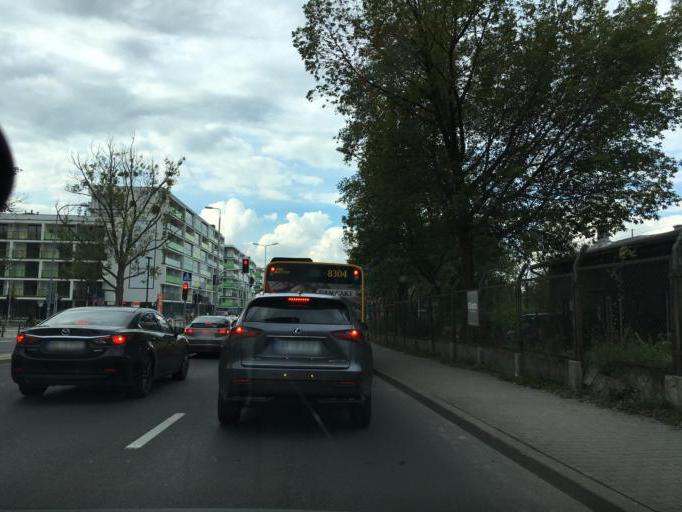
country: PL
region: Masovian Voivodeship
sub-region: Warszawa
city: Zoliborz
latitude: 52.2565
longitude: 20.9683
